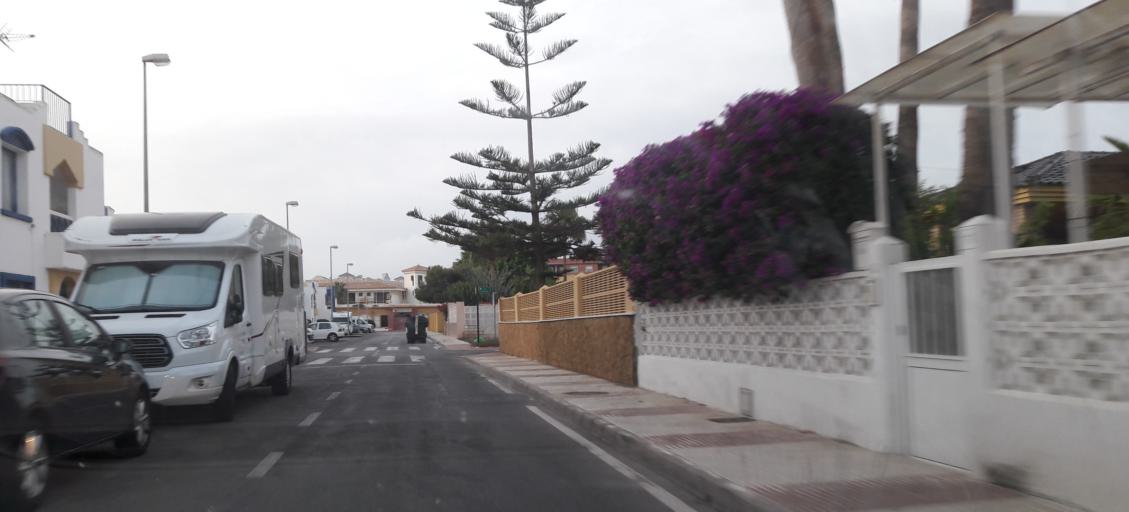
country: ES
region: Andalusia
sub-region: Provincia de Almeria
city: Roquetas de Mar
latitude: 36.7304
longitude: -2.6268
